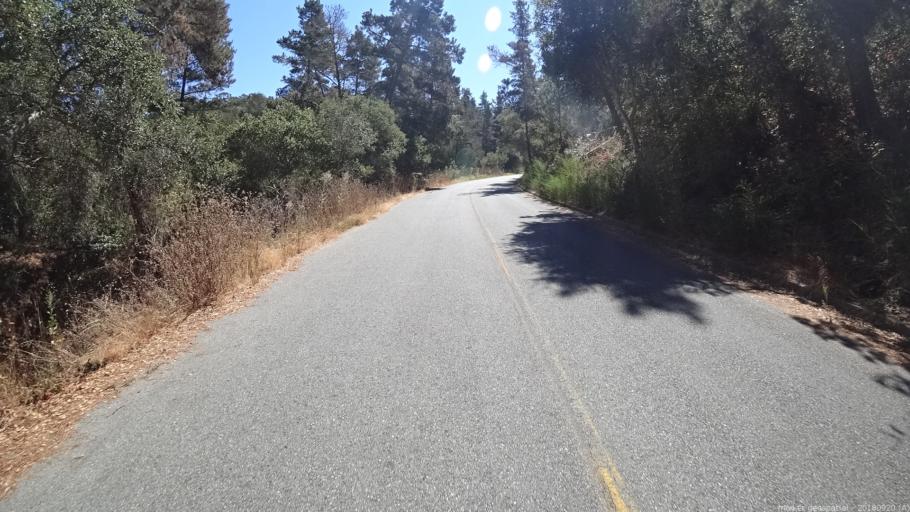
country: US
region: California
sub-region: Monterey County
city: Del Rey Oaks
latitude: 36.5724
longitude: -121.8566
